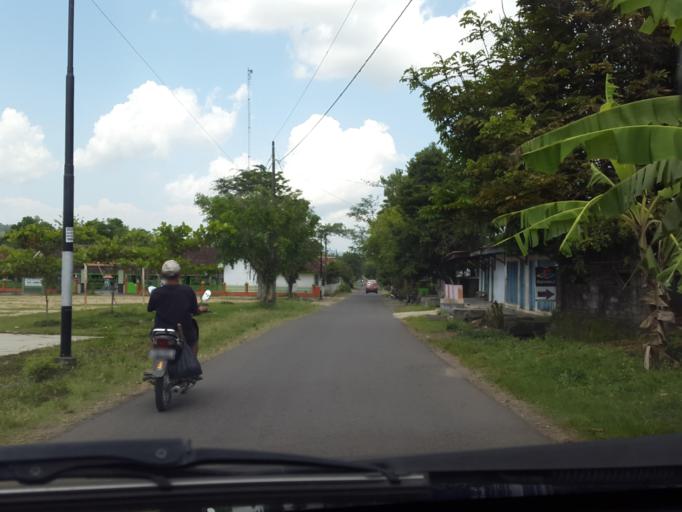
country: ID
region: Central Java
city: Selogiri
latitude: -7.8665
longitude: 110.7401
